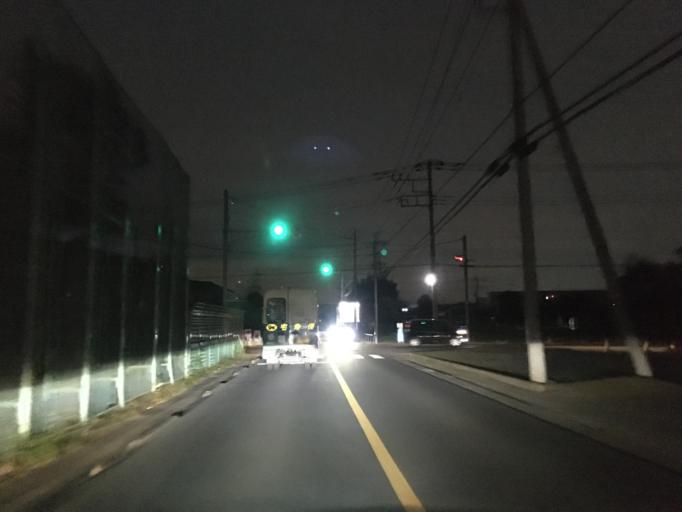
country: JP
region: Saitama
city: Sayama
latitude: 35.8870
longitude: 139.3824
